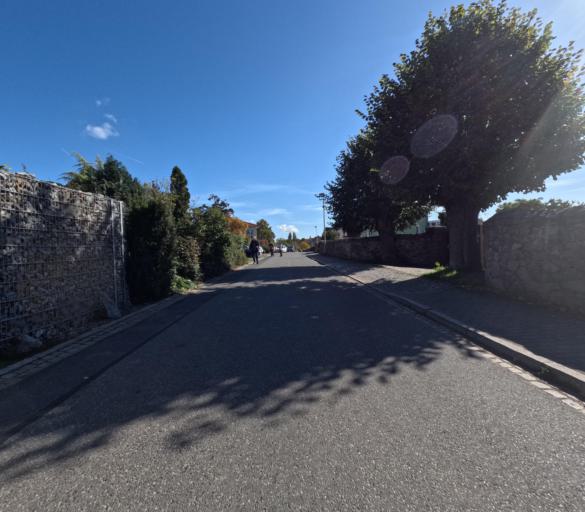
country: DE
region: Saxony
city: Radebeul
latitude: 51.1165
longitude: 13.6782
